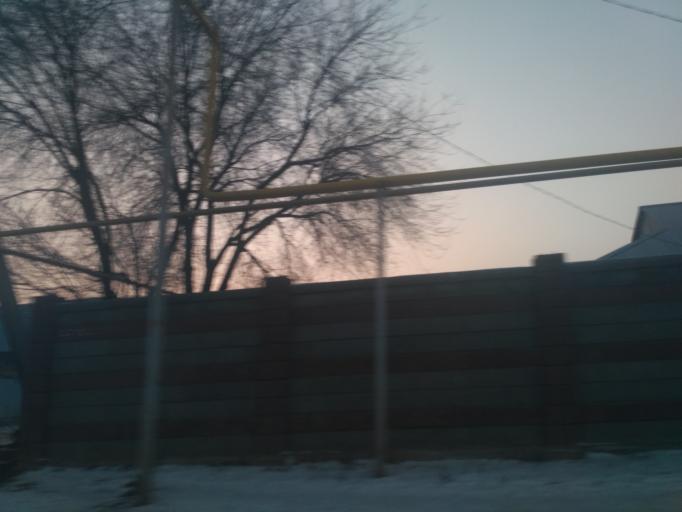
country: KZ
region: Almaty Oblysy
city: Burunday
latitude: 43.3717
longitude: 76.8392
